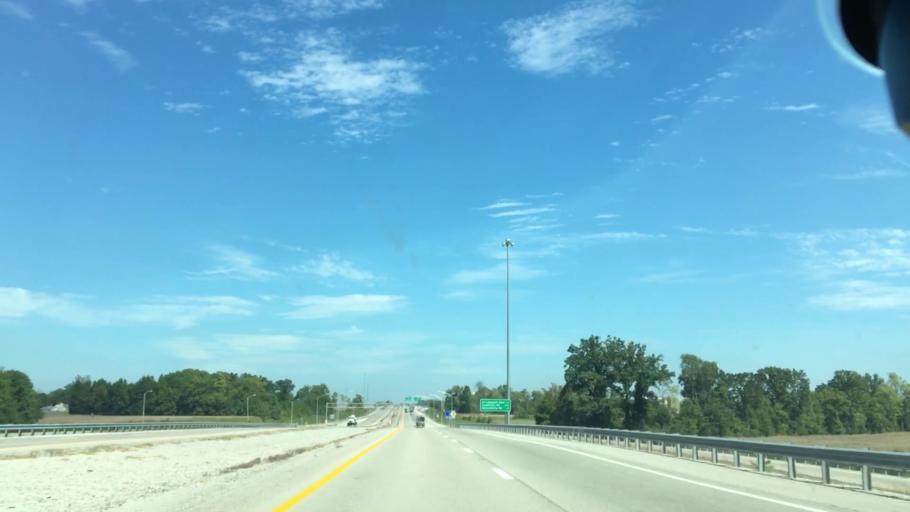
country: US
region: Kentucky
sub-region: Christian County
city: Hopkinsville
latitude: 36.8191
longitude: -87.4819
